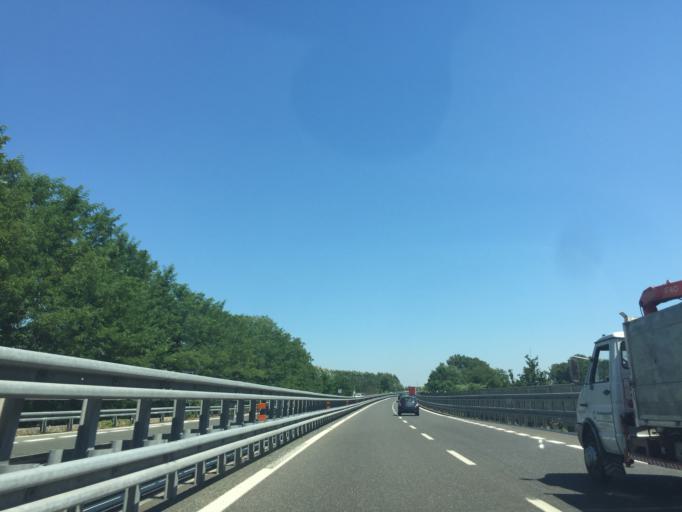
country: IT
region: Tuscany
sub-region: Provincia di Lucca
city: Lucca
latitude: 43.8526
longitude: 10.4328
